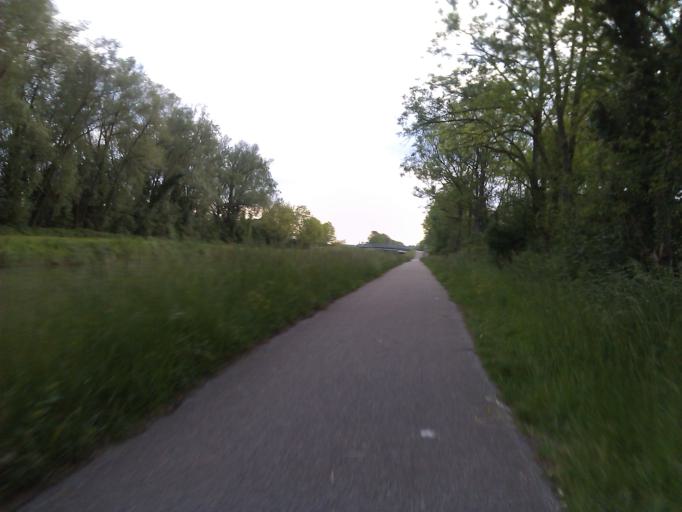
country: FR
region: Franche-Comte
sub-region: Departement du Jura
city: Dole
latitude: 47.0961
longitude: 5.5298
